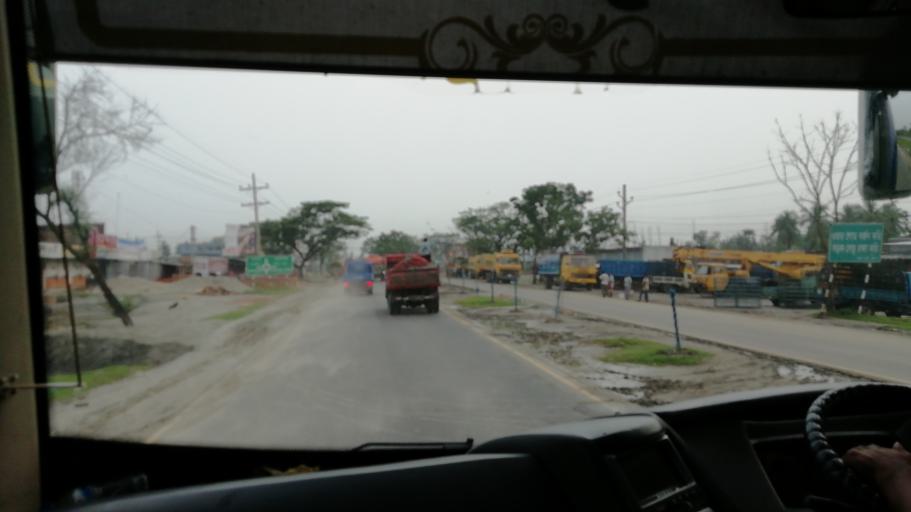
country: BD
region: Khulna
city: Khulna
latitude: 22.7963
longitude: 89.5296
